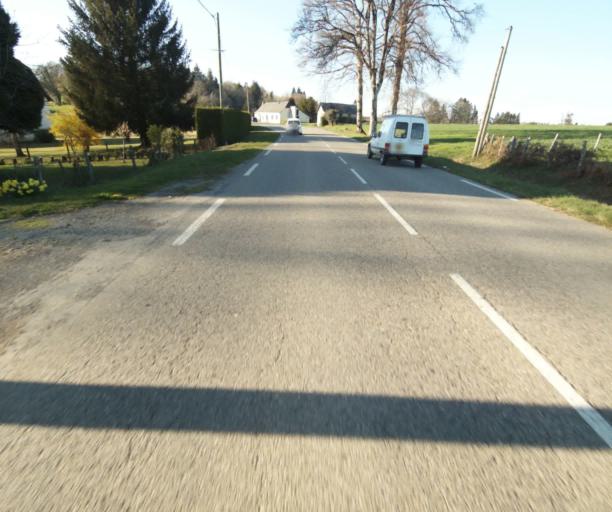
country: FR
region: Limousin
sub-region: Departement de la Correze
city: Seilhac
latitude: 45.3793
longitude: 1.7229
